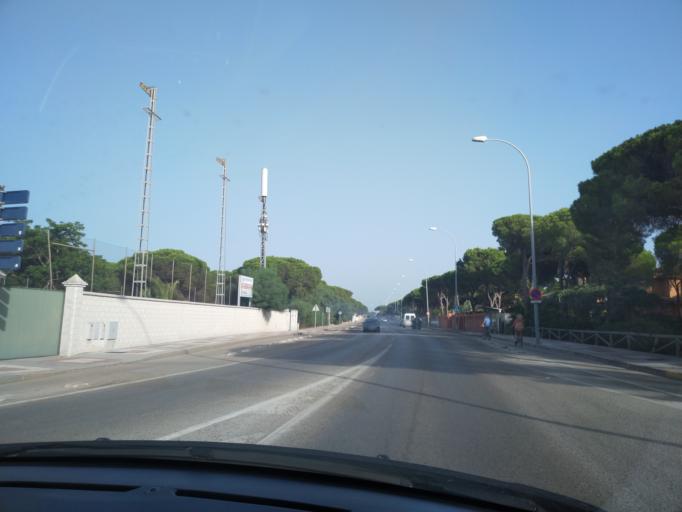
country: ES
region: Andalusia
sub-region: Provincia de Cadiz
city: Chiclana de la Frontera
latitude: 36.3803
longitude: -6.1916
